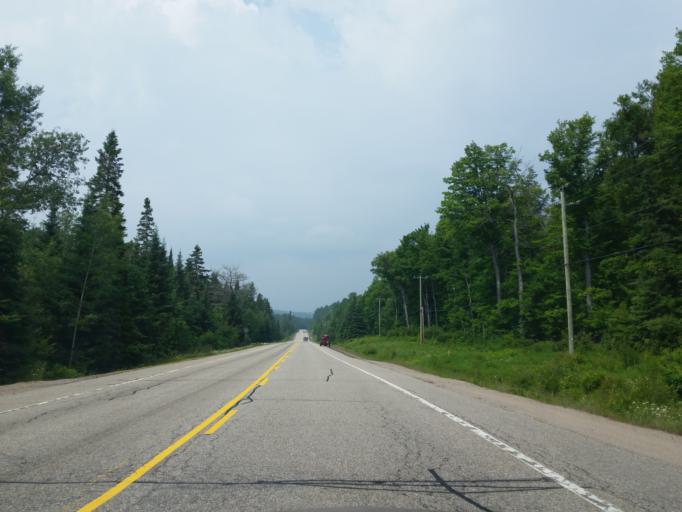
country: CA
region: Ontario
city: Mattawa
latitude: 45.5865
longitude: -78.4837
